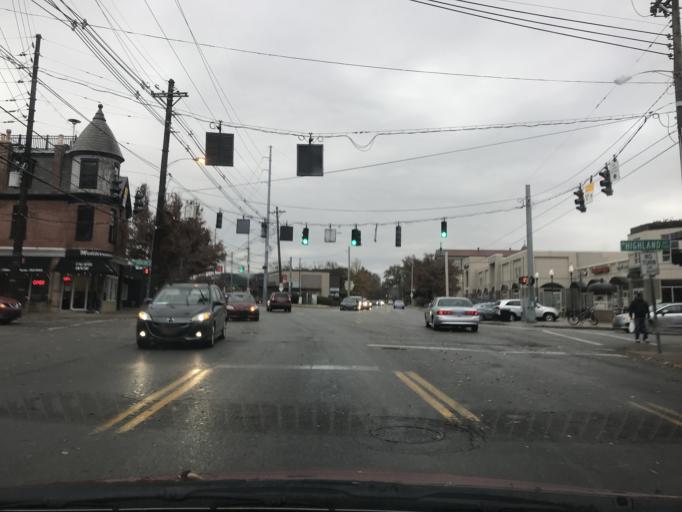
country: US
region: Kentucky
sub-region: Jefferson County
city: Audubon Park
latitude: 38.2405
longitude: -85.7244
